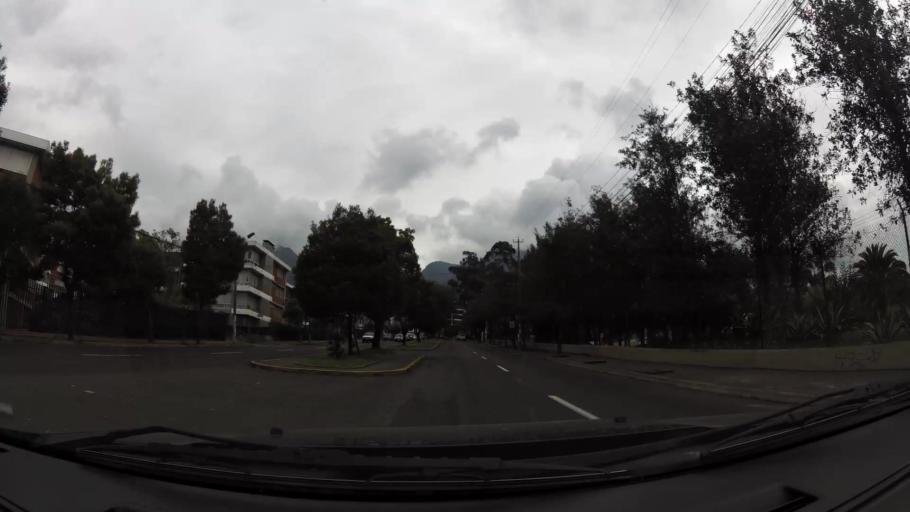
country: EC
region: Pichincha
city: Quito
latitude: -0.1845
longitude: -78.5001
